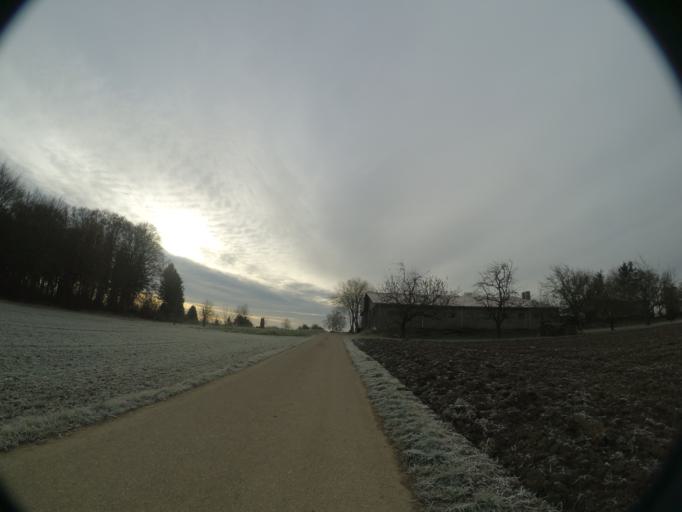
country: DE
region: Baden-Wuerttemberg
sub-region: Tuebingen Region
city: Beimerstetten
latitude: 48.4426
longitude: 10.0021
